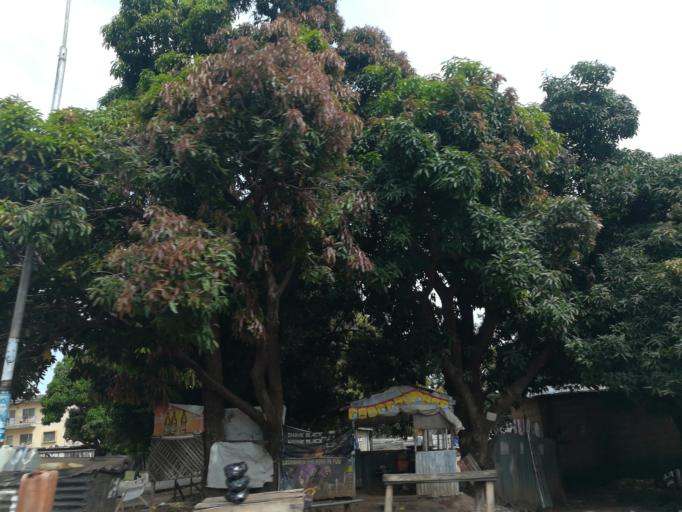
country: NG
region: Plateau
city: Jos
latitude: 9.9101
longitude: 8.8828
